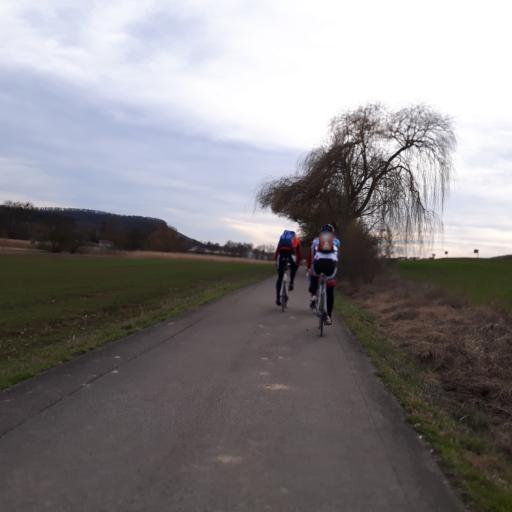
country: DE
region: Baden-Wuerttemberg
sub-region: Regierungsbezirk Stuttgart
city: Grossbottwar
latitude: 49.0105
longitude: 9.3055
